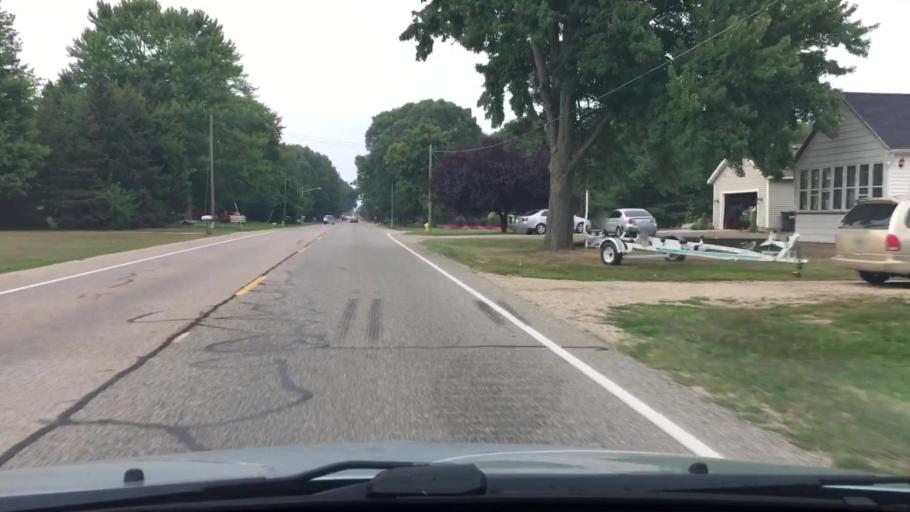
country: US
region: Michigan
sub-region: Ottawa County
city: Hudsonville
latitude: 42.8976
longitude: -85.9018
